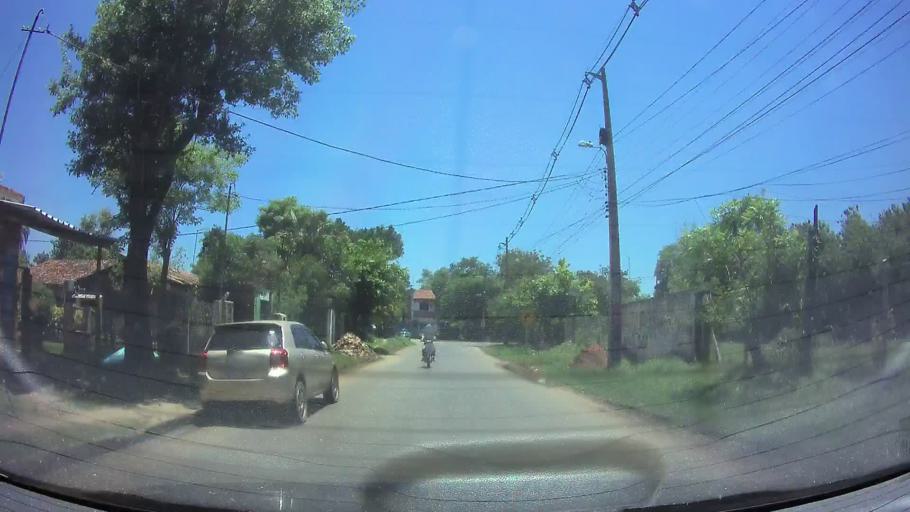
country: PY
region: Central
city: Fernando de la Mora
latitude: -25.2900
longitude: -57.5389
